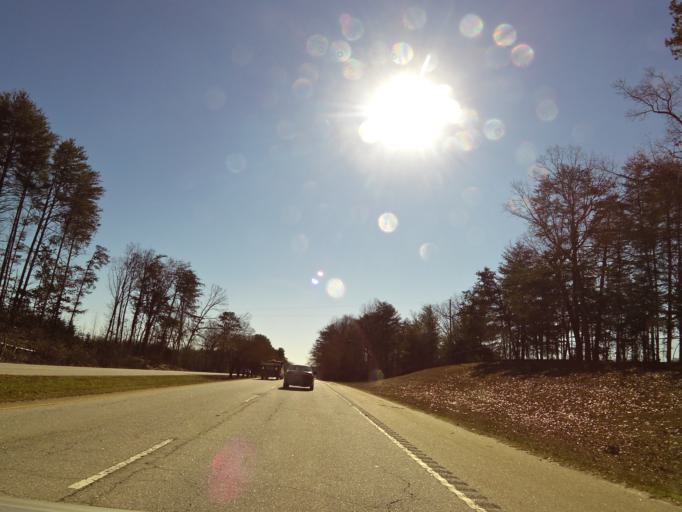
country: US
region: South Carolina
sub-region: Greenville County
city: Travelers Rest
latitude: 34.9312
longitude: -82.4332
